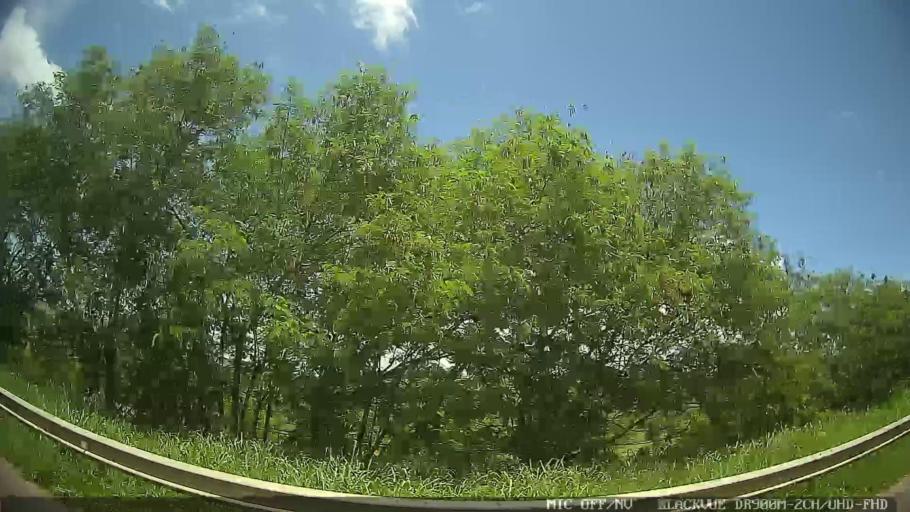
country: BR
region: Sao Paulo
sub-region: Laranjal Paulista
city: Laranjal Paulista
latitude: -23.0410
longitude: -47.8506
